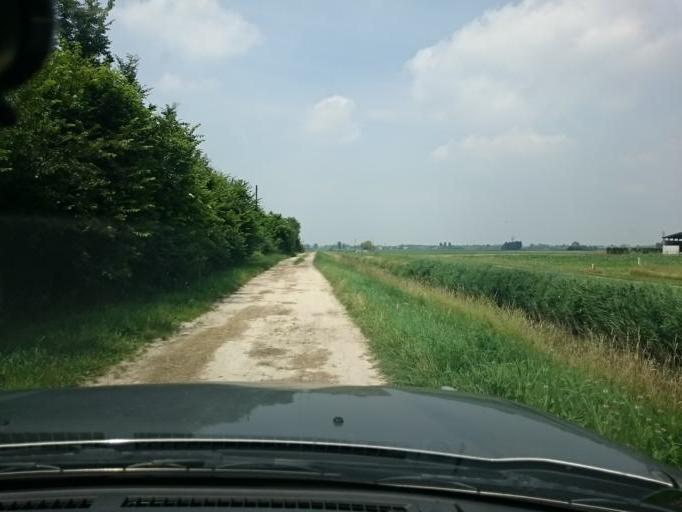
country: IT
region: Veneto
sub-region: Provincia di Padova
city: Correzzola
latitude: 45.2531
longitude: 12.0677
